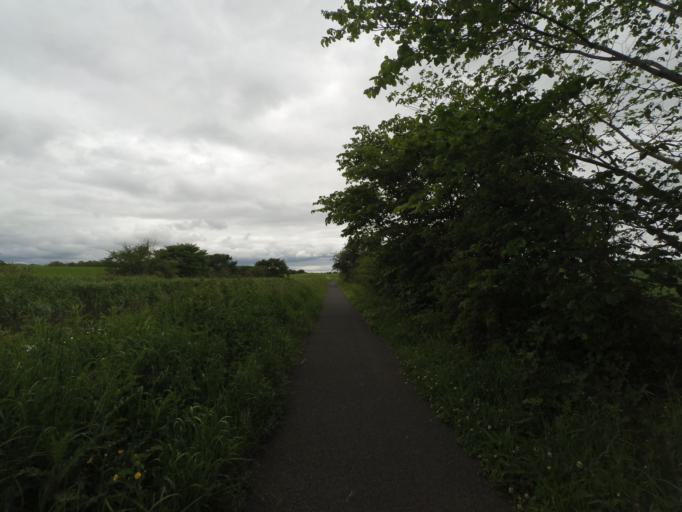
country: GB
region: Scotland
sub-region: West Lothian
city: Linlithgow
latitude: 55.9754
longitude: -3.5323
